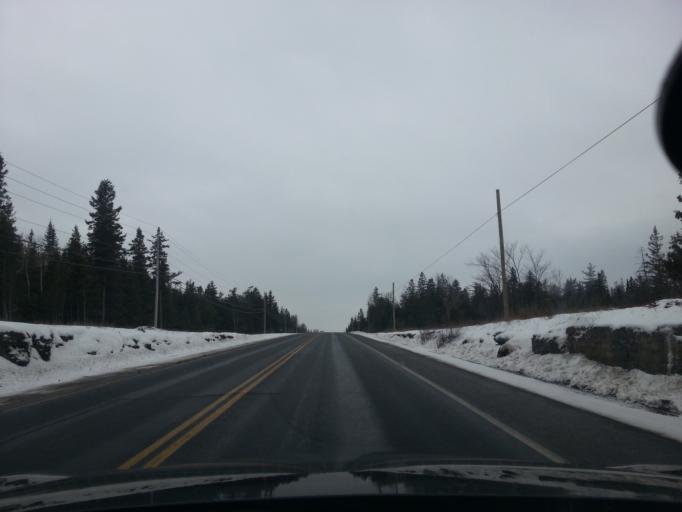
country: CA
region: Ontario
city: Carleton Place
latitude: 45.2643
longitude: -76.1341
